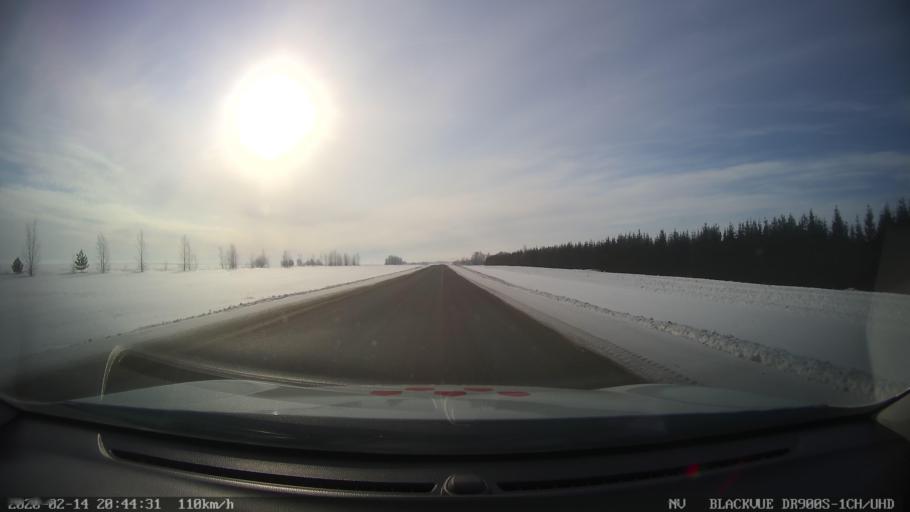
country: RU
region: Tatarstan
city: Kuybyshevskiy Zaton
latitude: 55.2926
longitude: 49.1458
